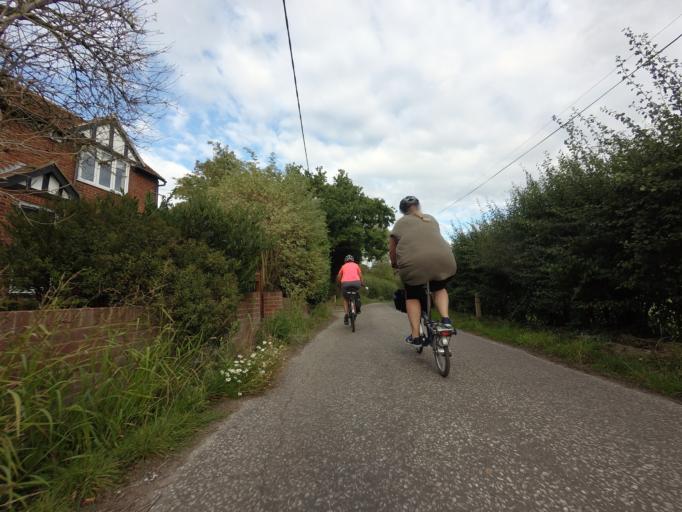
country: GB
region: England
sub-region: Kent
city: Staplehurst
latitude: 51.2111
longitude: 0.5547
